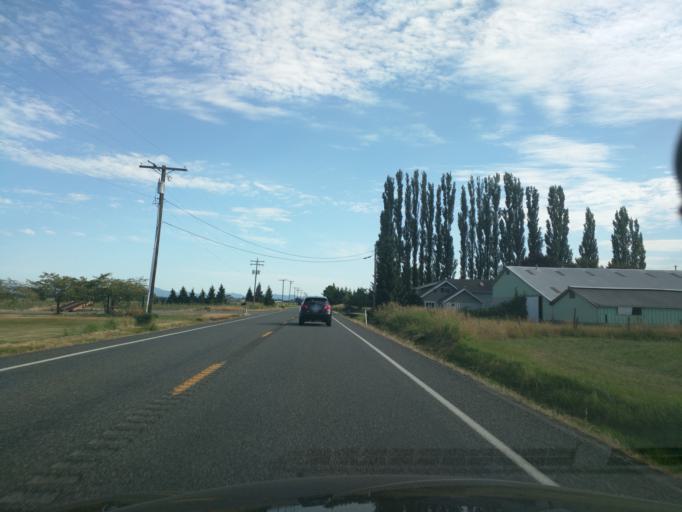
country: US
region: Washington
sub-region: Whatcom County
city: Lynden
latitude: 48.9810
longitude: -122.4852
